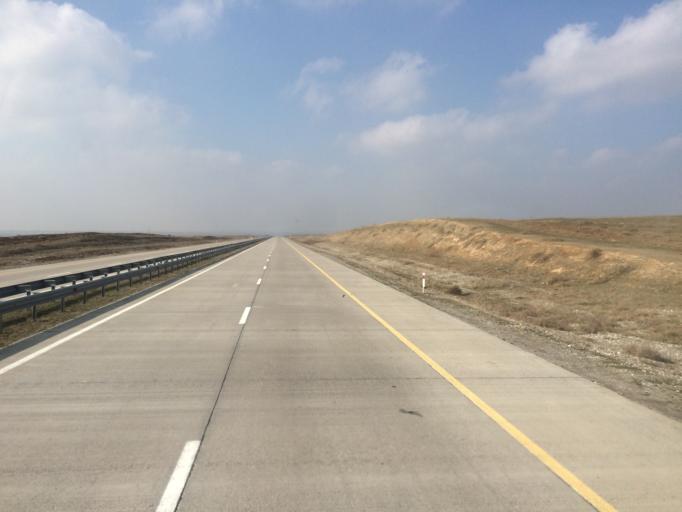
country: KZ
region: Ongtustik Qazaqstan
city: Temirlanovka
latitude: 42.5161
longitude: 69.4259
